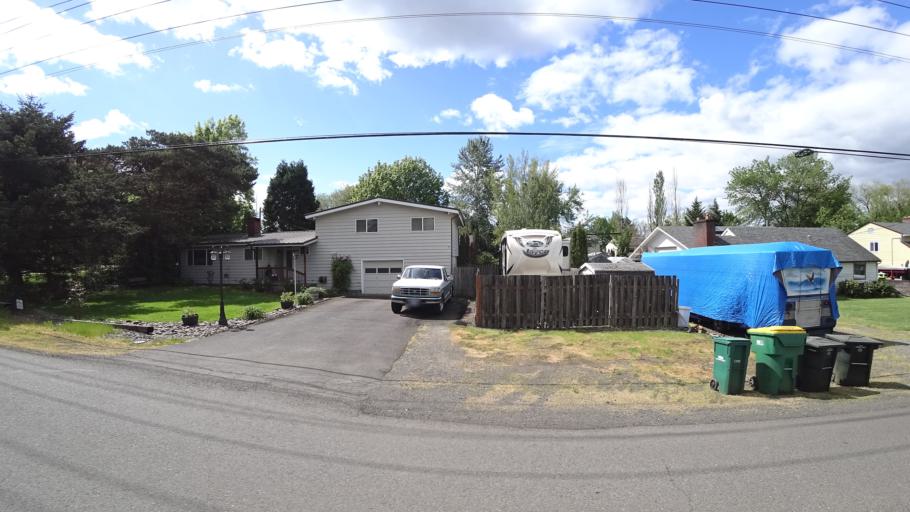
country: US
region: Oregon
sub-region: Washington County
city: Metzger
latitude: 45.4432
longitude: -122.7479
